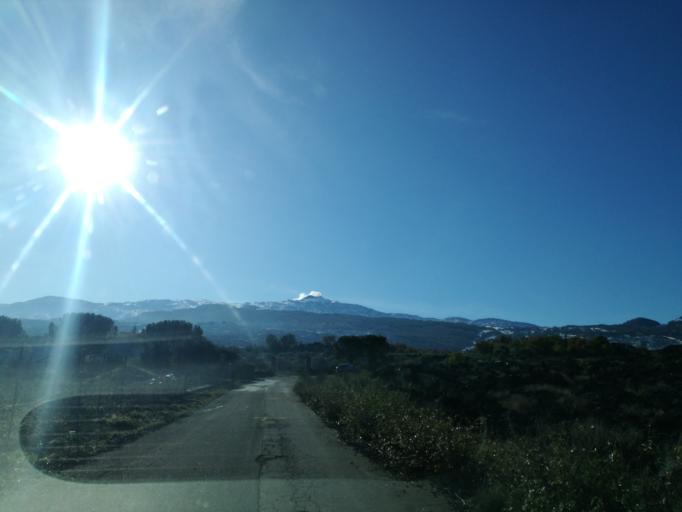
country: IT
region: Sicily
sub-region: Catania
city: Randazzo
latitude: 37.8656
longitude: 14.9800
